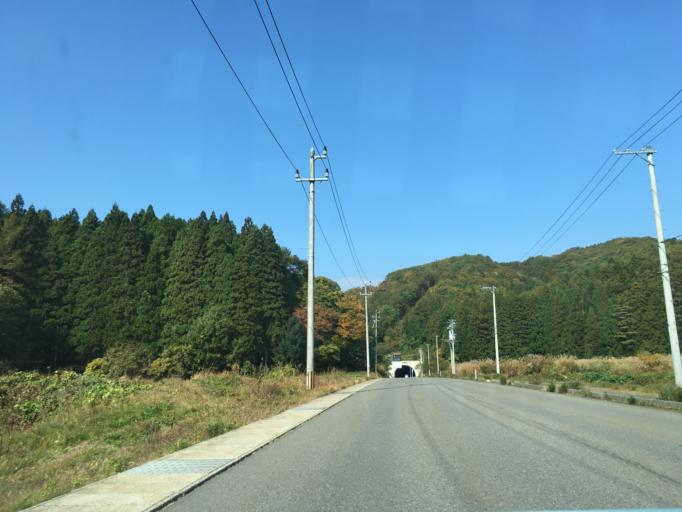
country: JP
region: Fukushima
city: Inawashiro
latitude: 37.4102
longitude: 140.0570
